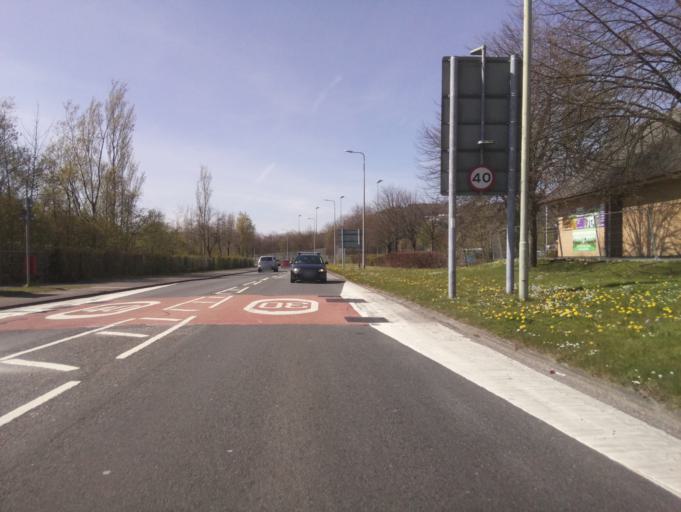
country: GB
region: Wales
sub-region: Rhondda Cynon Taf
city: Mountain Ash
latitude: 51.6858
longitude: -3.3819
